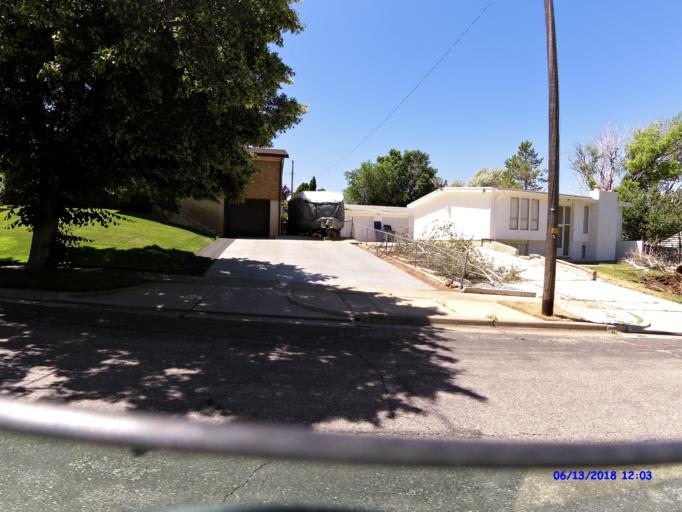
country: US
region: Utah
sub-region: Weber County
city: Ogden
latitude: 41.2301
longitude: -111.9327
